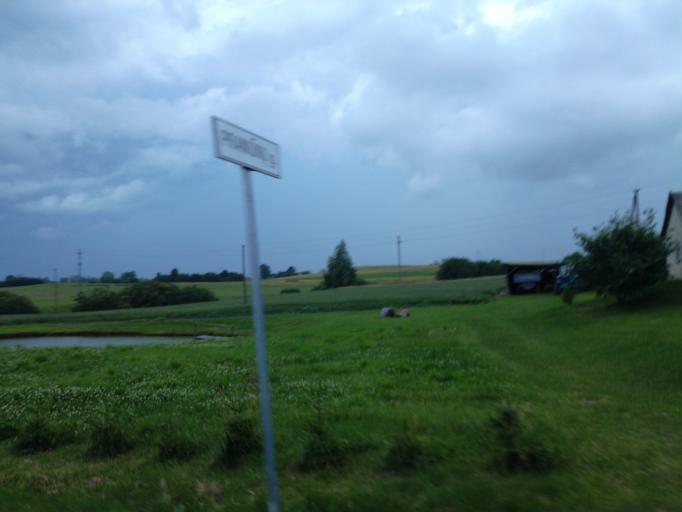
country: LT
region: Alytaus apskritis
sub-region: Alytus
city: Alytus
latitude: 54.4707
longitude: 24.0383
